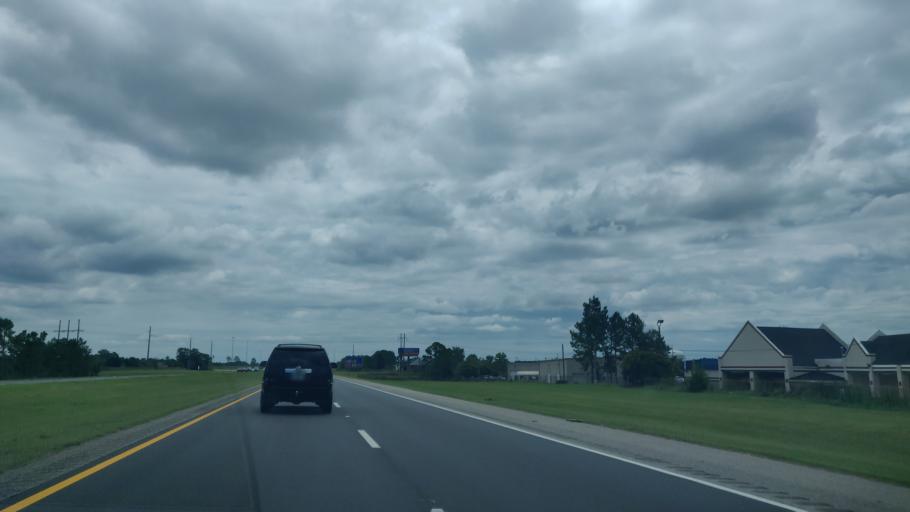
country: US
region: Georgia
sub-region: Dougherty County
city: Albany
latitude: 31.6205
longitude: -84.2150
